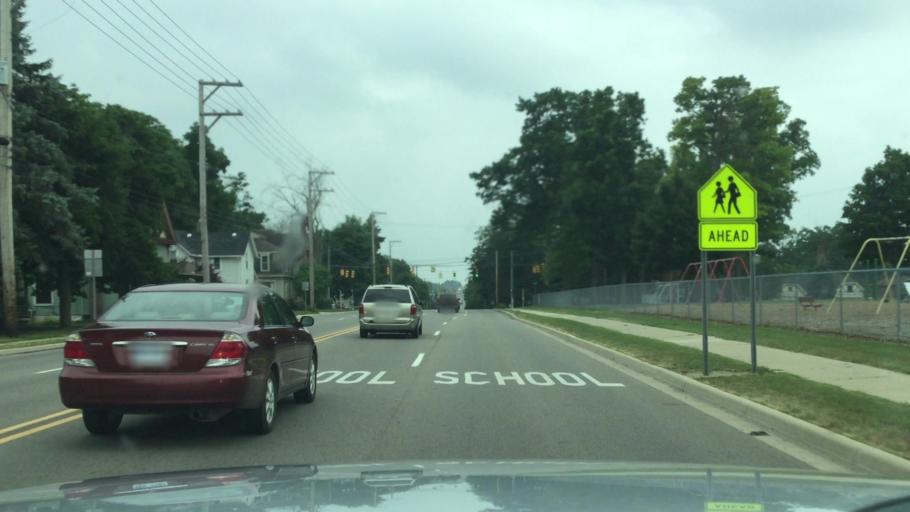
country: US
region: Michigan
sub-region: Shiawassee County
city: Owosso
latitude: 43.0032
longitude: -84.1769
